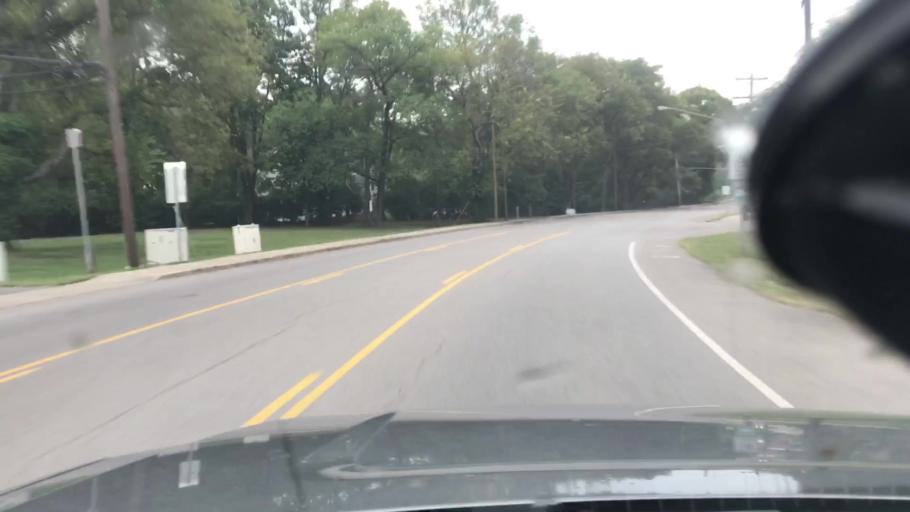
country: US
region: Tennessee
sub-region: Davidson County
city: Oak Hill
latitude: 36.1141
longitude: -86.7998
